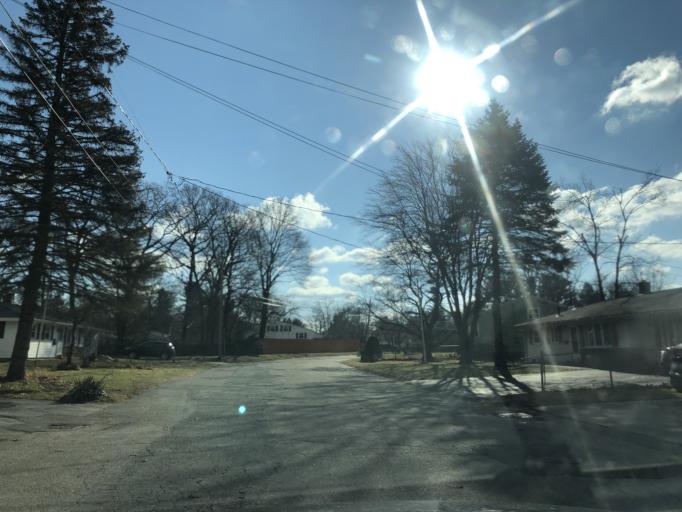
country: US
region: Massachusetts
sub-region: Plymouth County
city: Brockton
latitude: 42.1095
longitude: -71.0055
